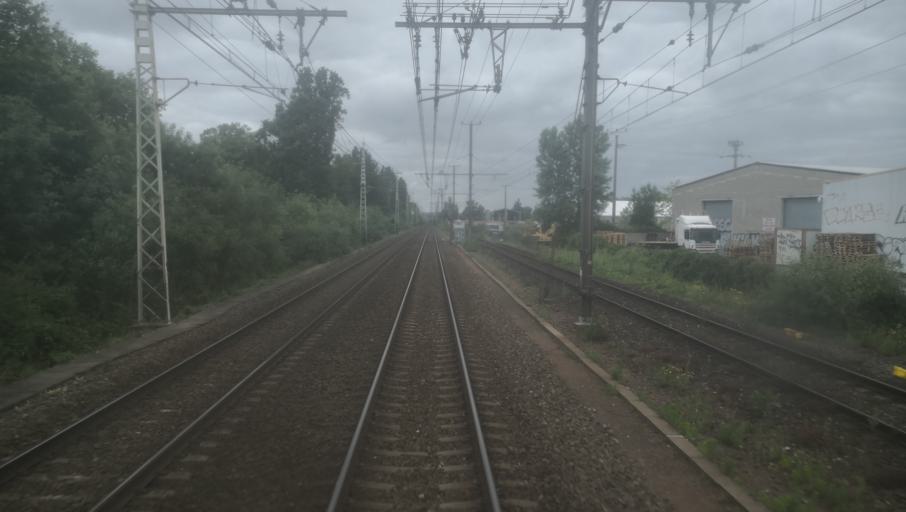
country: FR
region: Midi-Pyrenees
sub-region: Departement de la Haute-Garonne
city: Lespinasse
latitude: 43.7204
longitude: 1.3817
